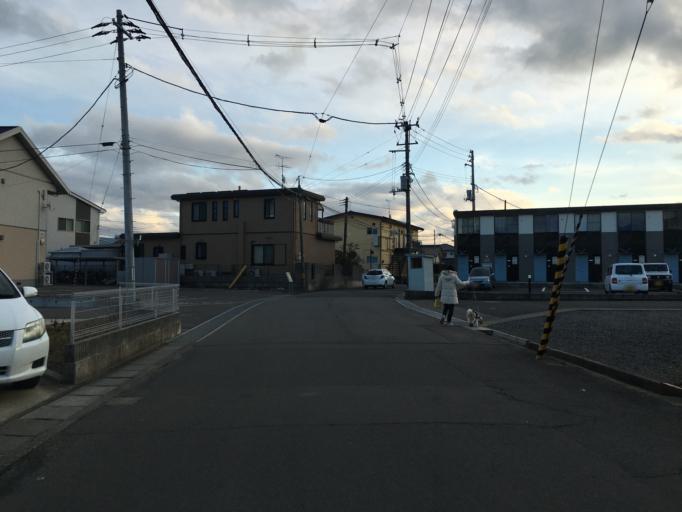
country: JP
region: Fukushima
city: Hobaramachi
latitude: 37.8074
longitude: 140.4901
